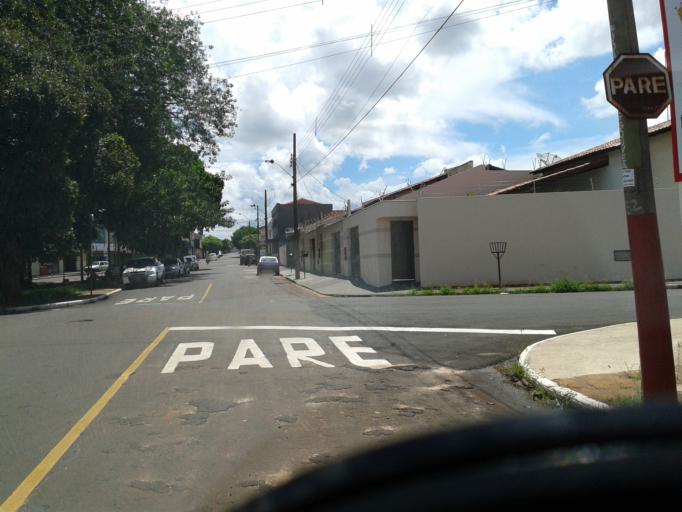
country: BR
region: Minas Gerais
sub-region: Ituiutaba
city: Ituiutaba
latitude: -18.9765
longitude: -49.4721
